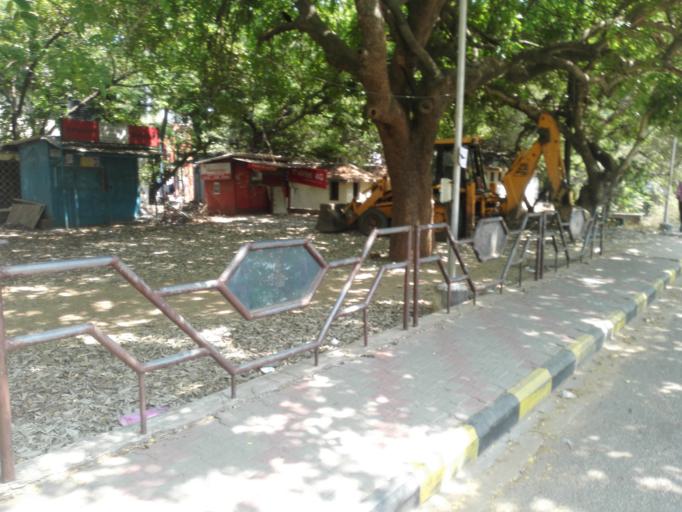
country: IN
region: Tamil Nadu
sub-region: Chennai
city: Gandhi Nagar
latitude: 13.0104
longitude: 80.2363
